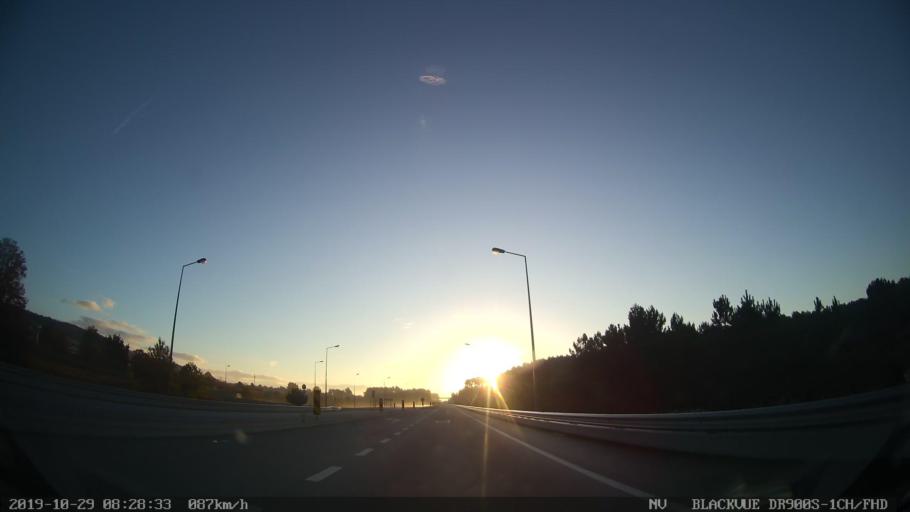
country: PT
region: Vila Real
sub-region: Sabrosa
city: Vilela
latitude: 41.2659
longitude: -7.6363
